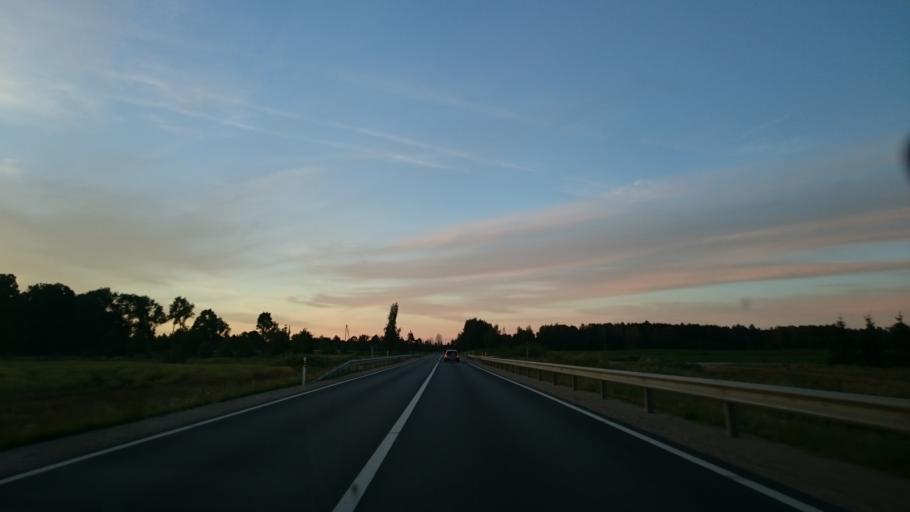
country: LV
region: Dobeles Rajons
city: Dobele
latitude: 56.7112
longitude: 23.1871
